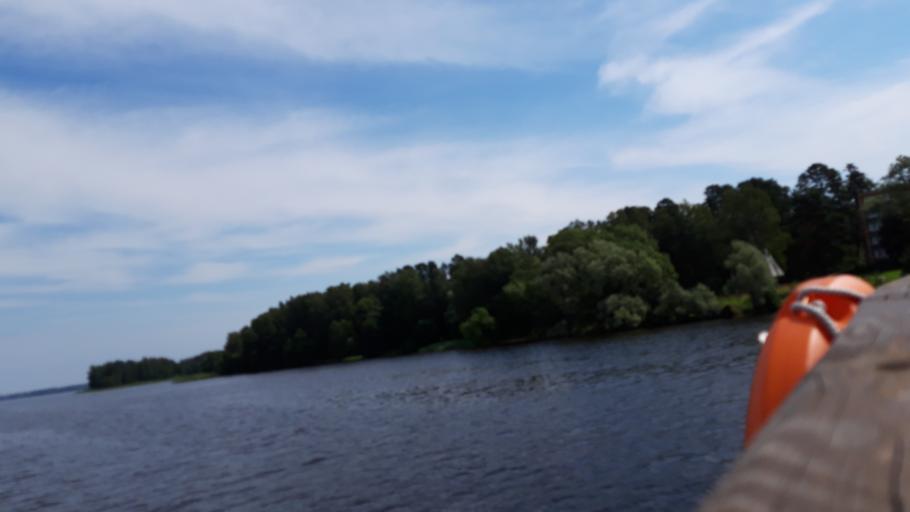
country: RU
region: Tverskaya
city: Konakovo
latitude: 56.6910
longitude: 36.6975
